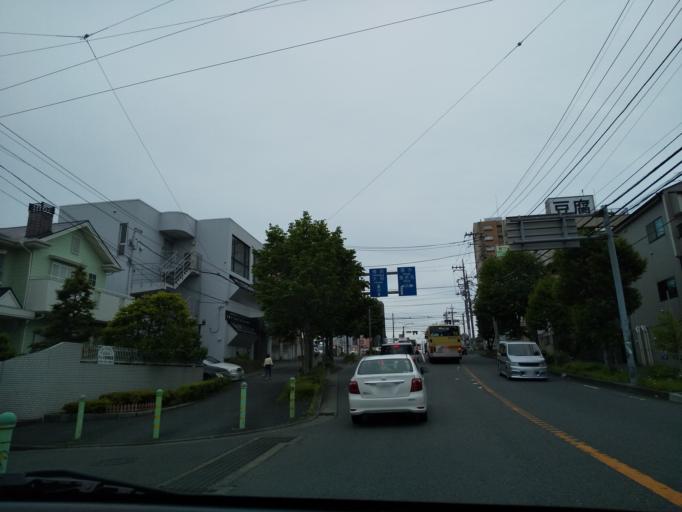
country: JP
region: Kanagawa
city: Zama
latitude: 35.5089
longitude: 139.4135
